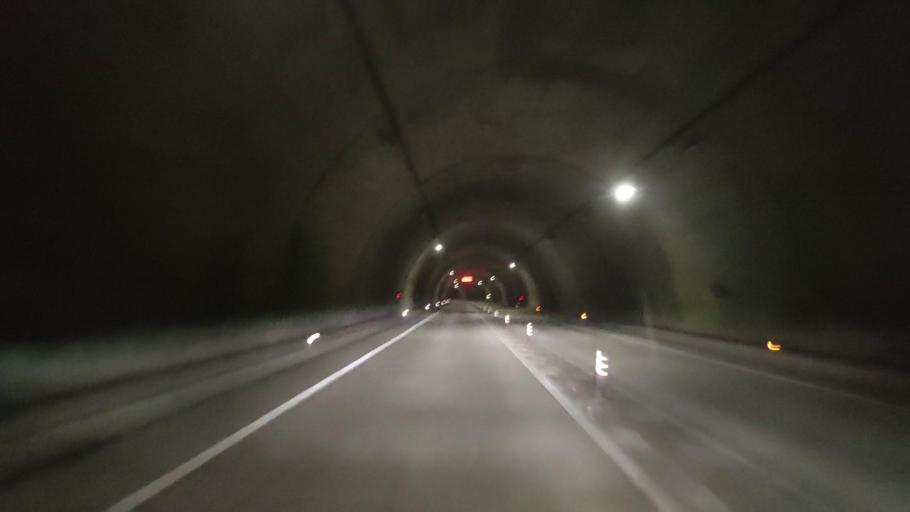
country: JP
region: Wakayama
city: Shingu
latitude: 33.7202
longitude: 135.9759
